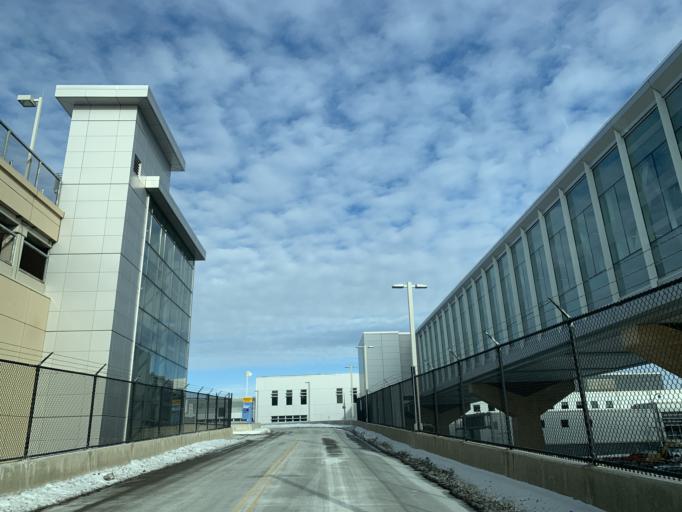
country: US
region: Minnesota
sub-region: Dakota County
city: Mendota Heights
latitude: 44.8797
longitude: -93.2021
